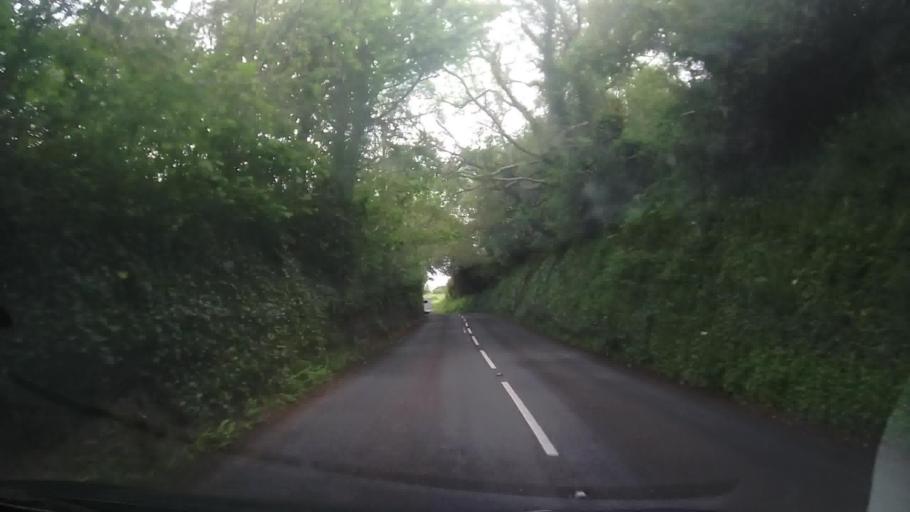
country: GB
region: England
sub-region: Devon
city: Kingsbridge
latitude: 50.2723
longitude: -3.7610
